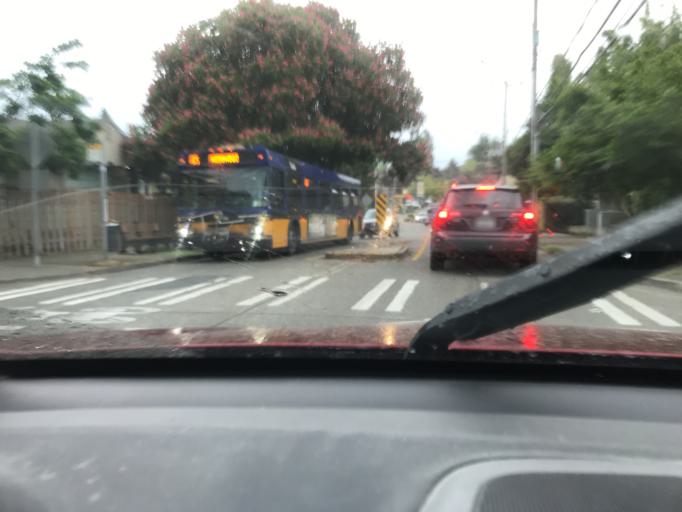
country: US
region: Washington
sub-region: King County
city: Yarrow Point
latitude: 47.6685
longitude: -122.2860
